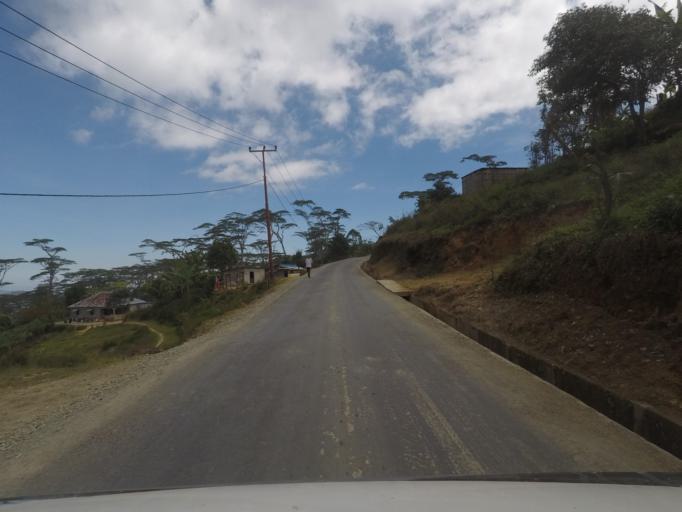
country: TL
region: Ermera
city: Gleno
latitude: -8.7502
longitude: 125.3554
